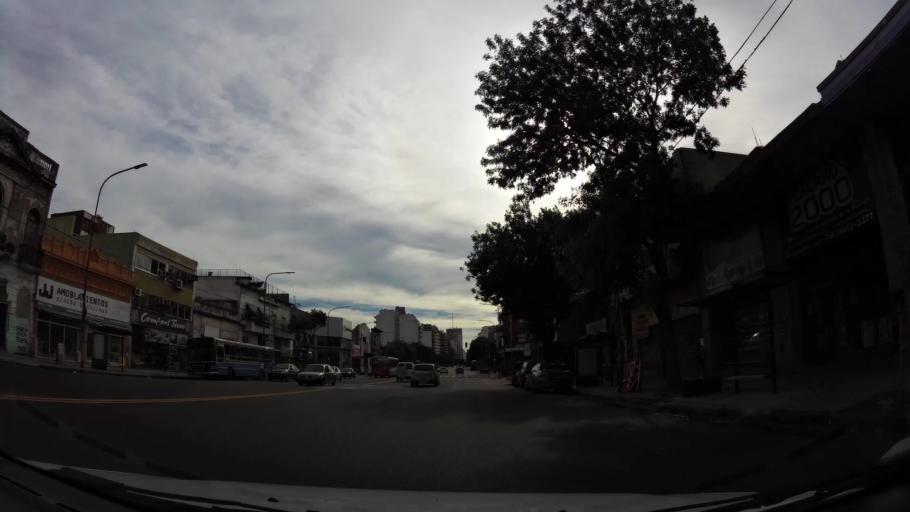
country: AR
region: Buenos Aires F.D.
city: Villa Santa Rita
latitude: -34.6314
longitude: -58.4727
